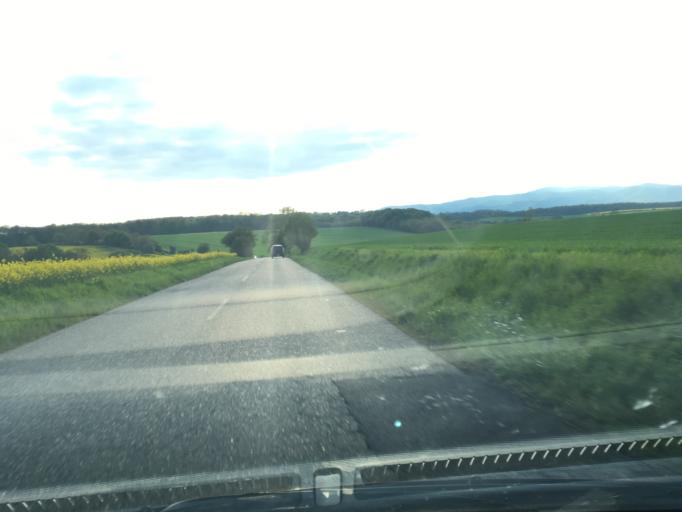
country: HU
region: Nograd
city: Retsag
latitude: 47.8847
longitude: 19.1186
